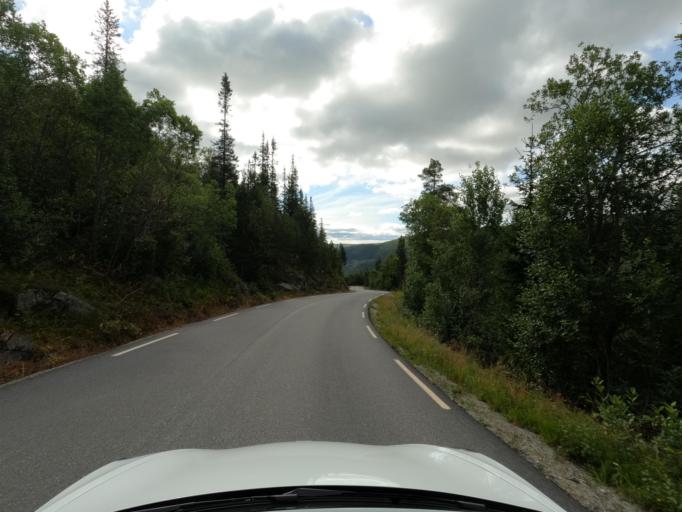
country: NO
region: Telemark
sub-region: Tinn
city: Rjukan
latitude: 60.1425
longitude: 8.6421
